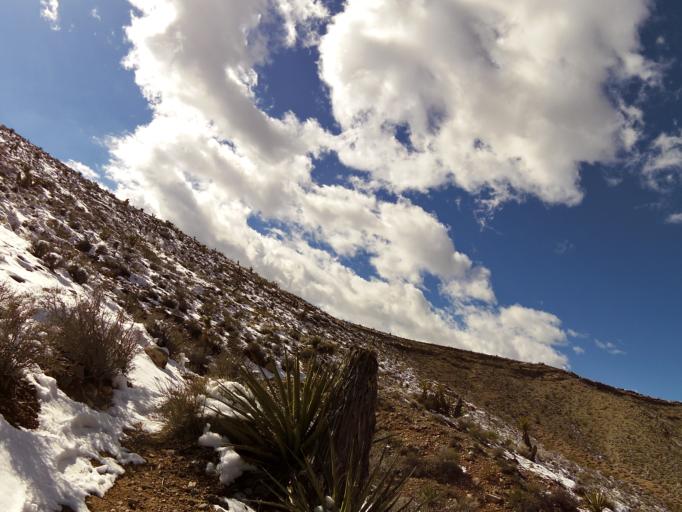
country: US
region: Nevada
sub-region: Clark County
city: Summerlin South
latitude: 36.1413
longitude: -115.4228
